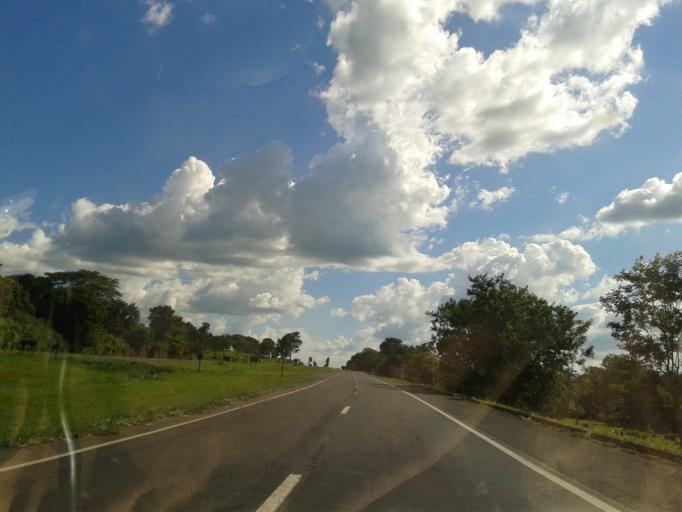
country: BR
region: Goias
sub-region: Goiatuba
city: Goiatuba
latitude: -18.1250
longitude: -49.2833
